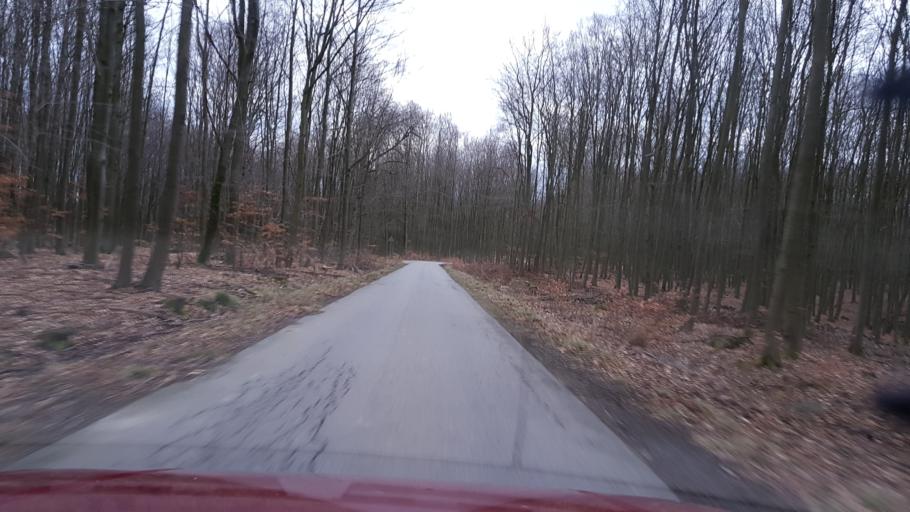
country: PL
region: West Pomeranian Voivodeship
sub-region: Powiat gryfinski
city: Stare Czarnowo
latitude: 53.3125
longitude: 14.7209
